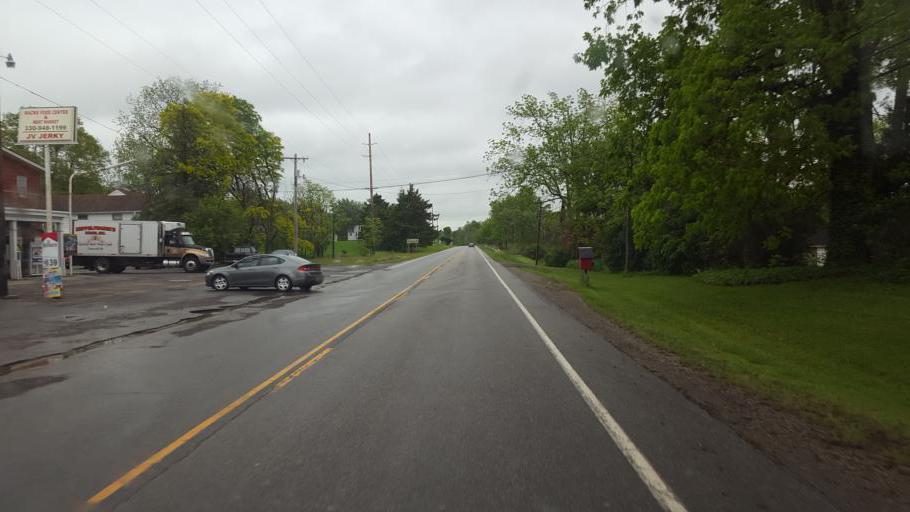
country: US
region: Ohio
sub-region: Medina County
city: Lodi
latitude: 41.0265
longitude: -82.0490
